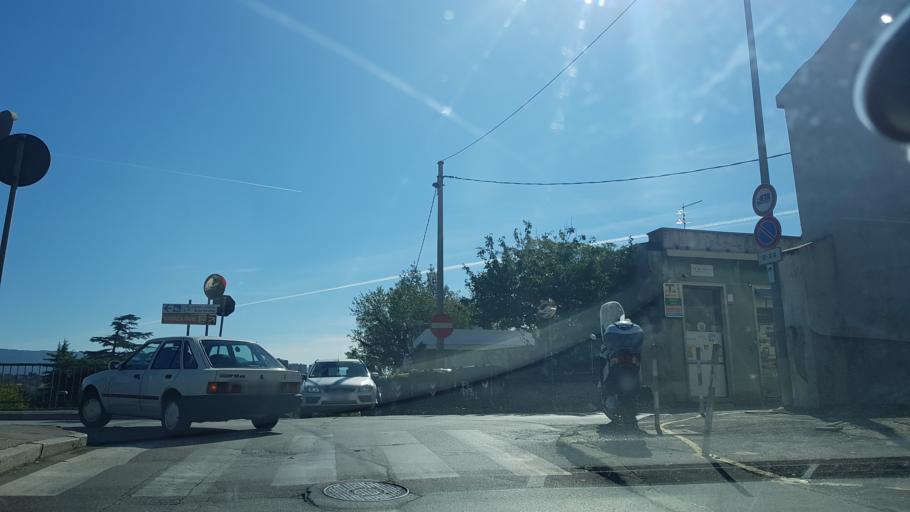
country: IT
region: Friuli Venezia Giulia
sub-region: Provincia di Trieste
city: Trieste
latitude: 45.6309
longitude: 13.7923
